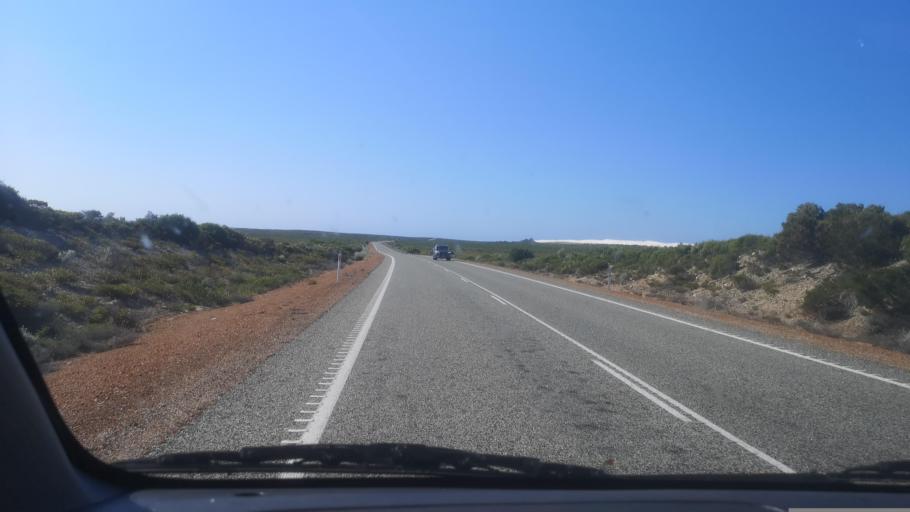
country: AU
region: Western Australia
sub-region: Dandaragan
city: Jurien Bay
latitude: -30.7403
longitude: 115.1850
